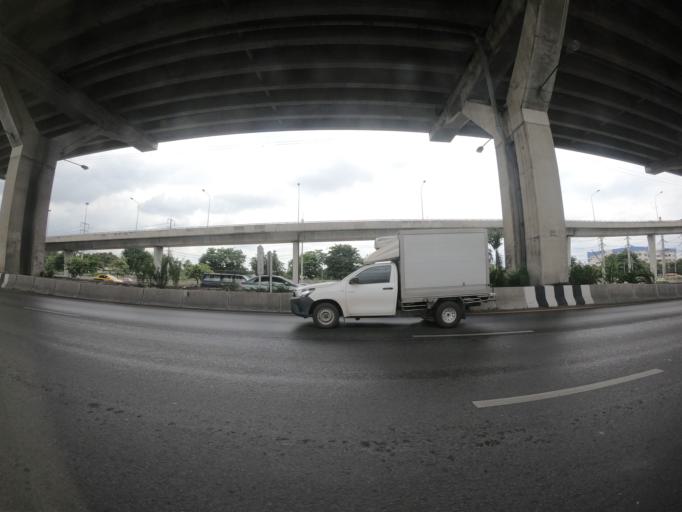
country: TH
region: Bangkok
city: Sai Mai
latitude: 13.9803
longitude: 100.6210
